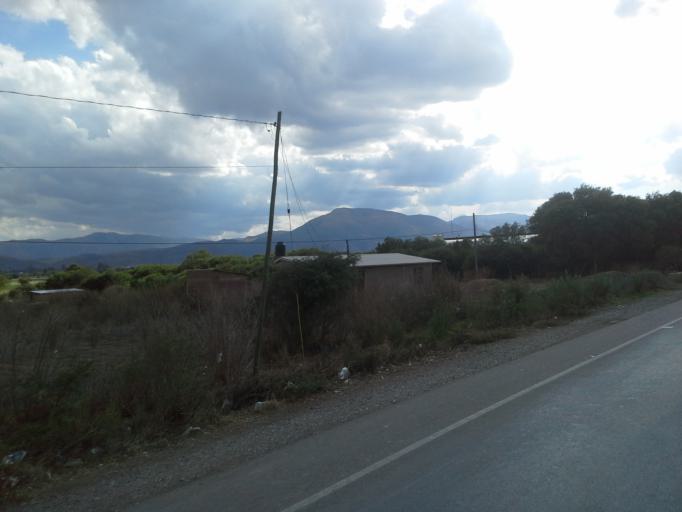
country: BO
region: Cochabamba
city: Tarata
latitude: -17.5442
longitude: -66.0183
